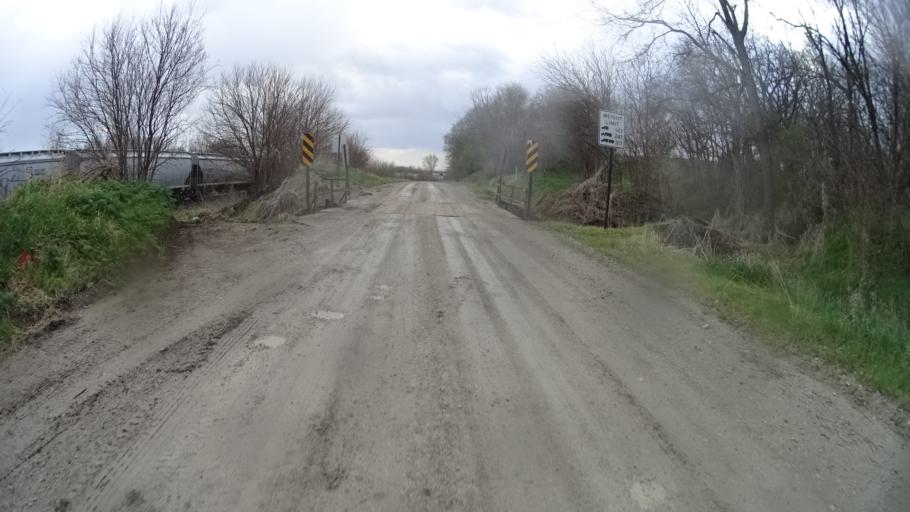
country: US
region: Nebraska
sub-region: Sarpy County
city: Offutt Air Force Base
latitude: 41.0855
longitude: -95.9163
